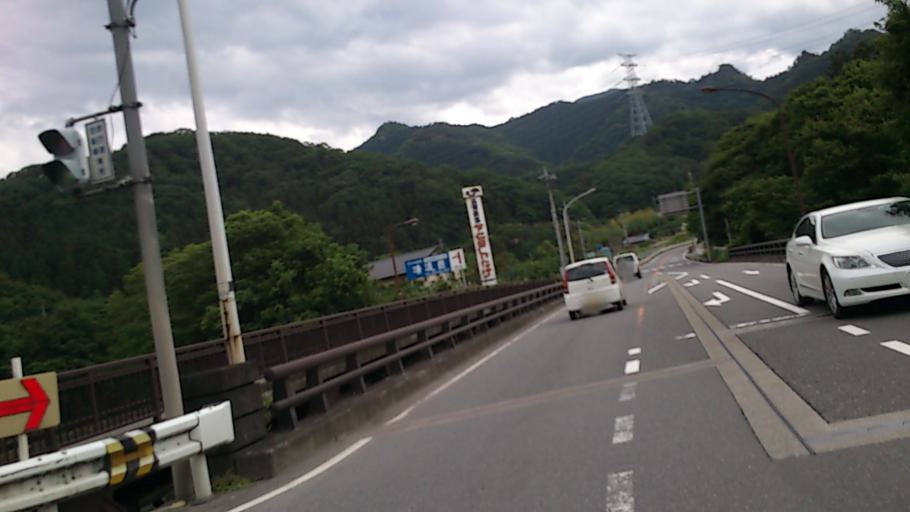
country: JP
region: Gunma
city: Tomioka
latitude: 36.2169
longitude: 138.8034
